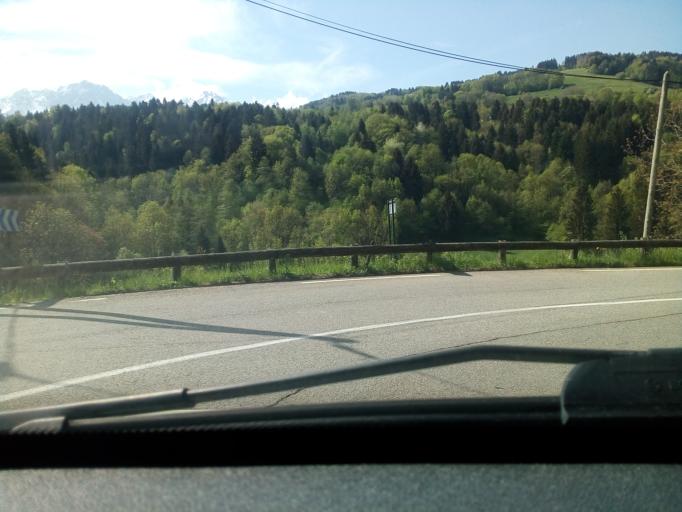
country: FR
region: Rhone-Alpes
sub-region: Departement de l'Isere
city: Le Champ-pres-Froges
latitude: 45.2696
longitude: 5.9682
